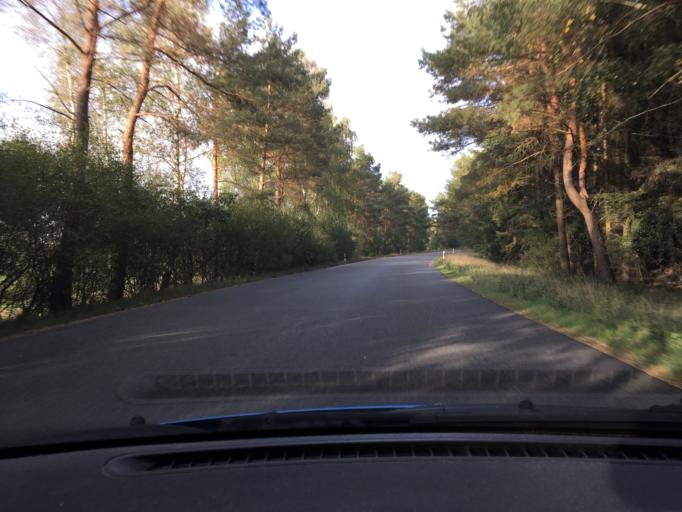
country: DE
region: Lower Saxony
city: Soltau
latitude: 52.9639
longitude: 9.9113
